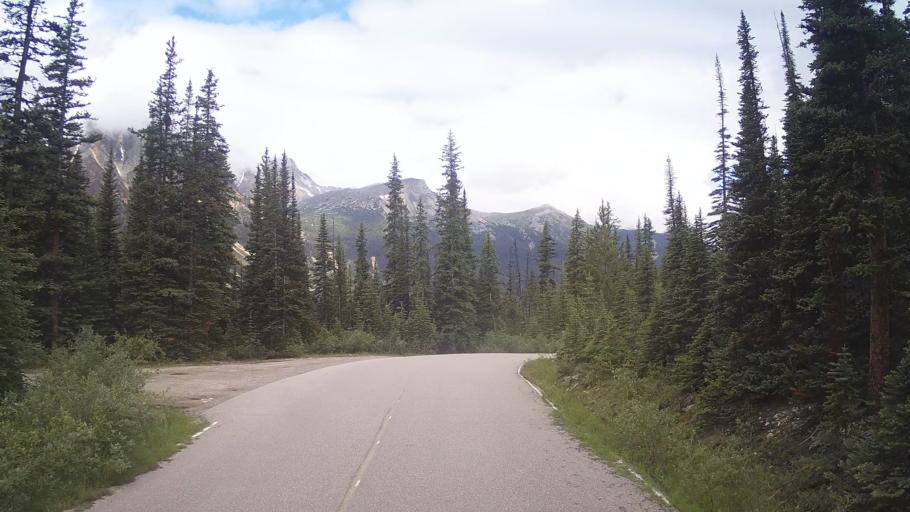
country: CA
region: Alberta
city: Jasper Park Lodge
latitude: 52.7003
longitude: -118.0594
